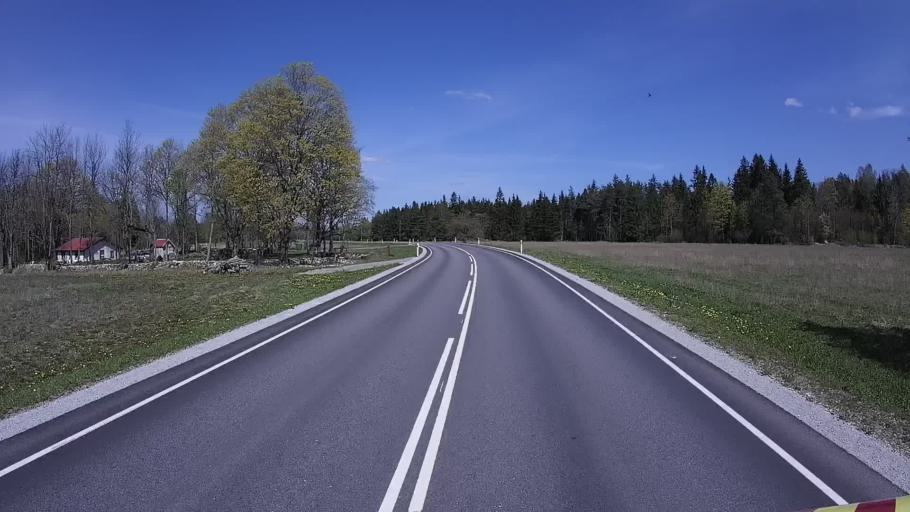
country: EE
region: Harju
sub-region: Paldiski linn
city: Paldiski
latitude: 59.1978
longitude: 24.0966
